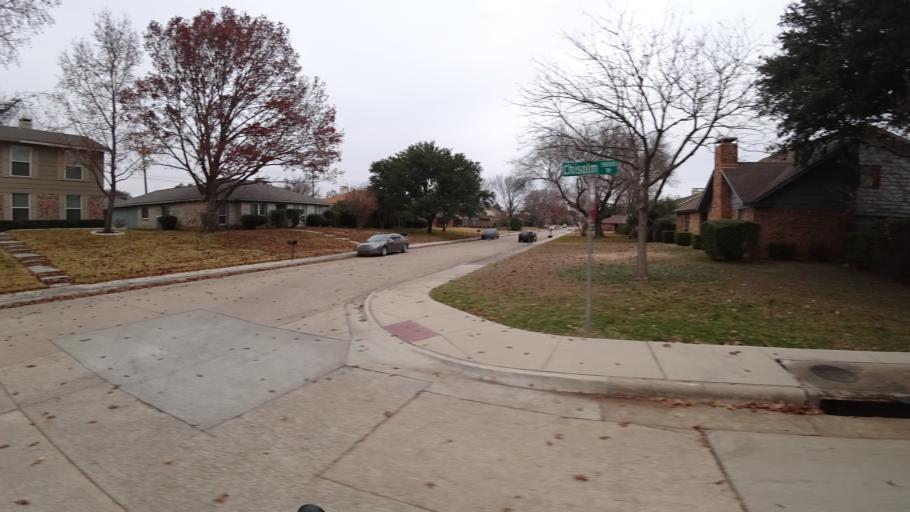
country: US
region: Texas
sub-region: Denton County
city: Highland Village
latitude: 33.0520
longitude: -97.0438
